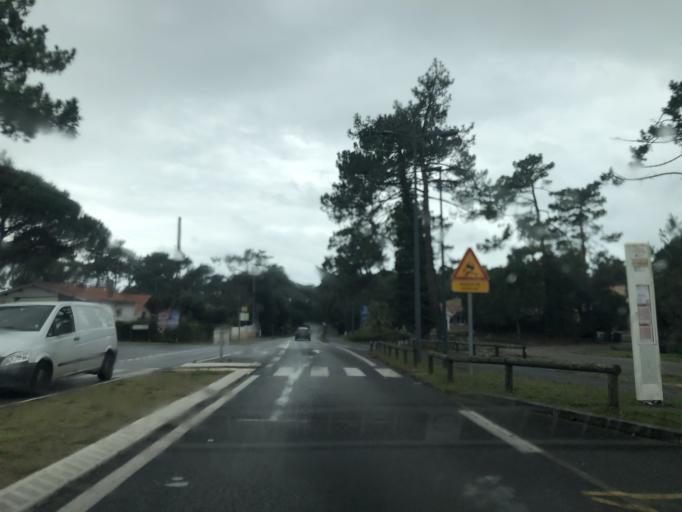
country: FR
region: Aquitaine
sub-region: Departement de la Gironde
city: Arcachon
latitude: 44.6940
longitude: -1.2356
